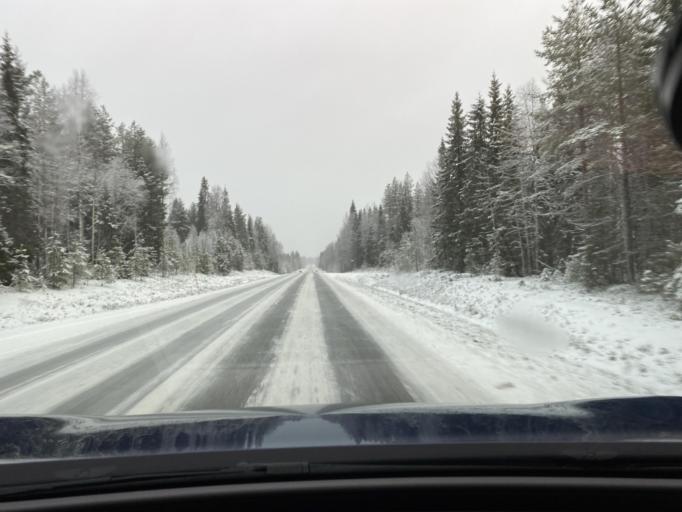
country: FI
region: Northern Ostrobothnia
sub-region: Oulu
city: Yli-Ii
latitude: 65.9426
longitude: 25.8925
